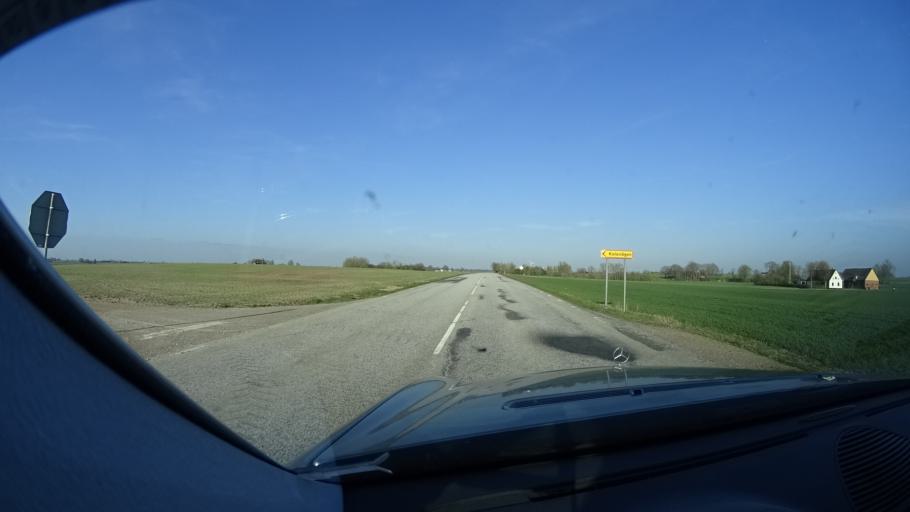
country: SE
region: Skane
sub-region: Eslovs Kommun
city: Eslov
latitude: 55.8560
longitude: 13.2051
